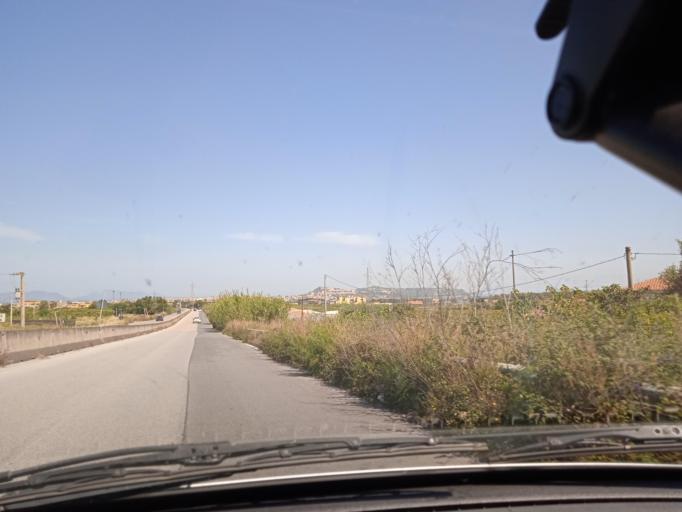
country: IT
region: Sicily
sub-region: Messina
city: San Filippo del Mela
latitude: 38.1885
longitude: 15.2624
